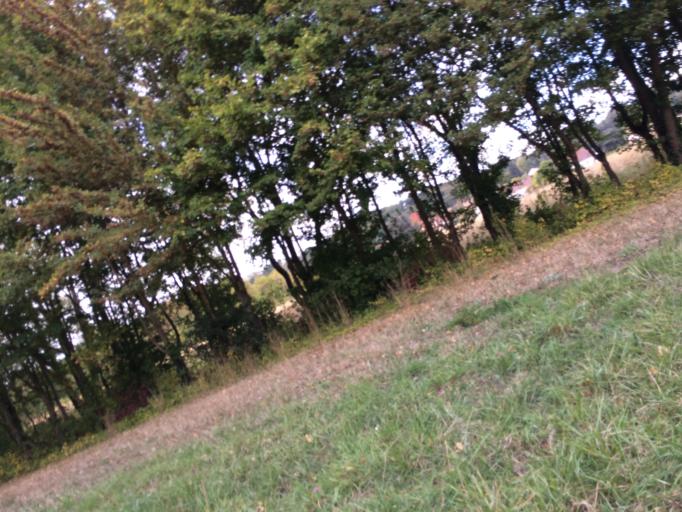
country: FR
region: Ile-de-France
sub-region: Departement de l'Essonne
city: Linas
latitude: 48.6374
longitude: 2.2582
